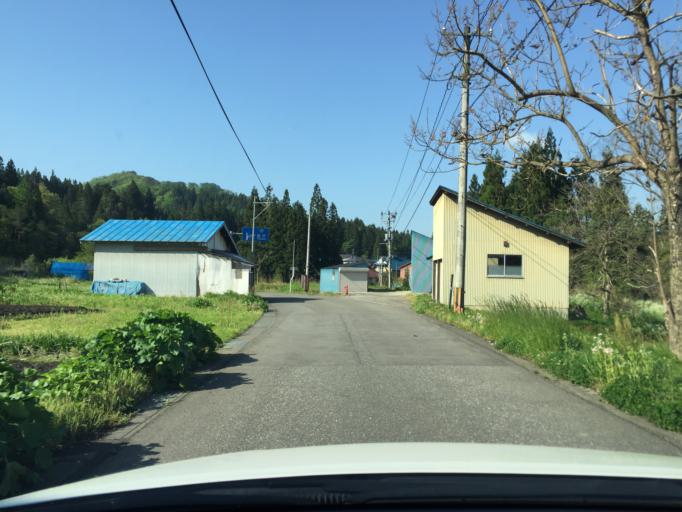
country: JP
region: Fukushima
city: Kitakata
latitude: 37.6750
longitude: 139.6484
